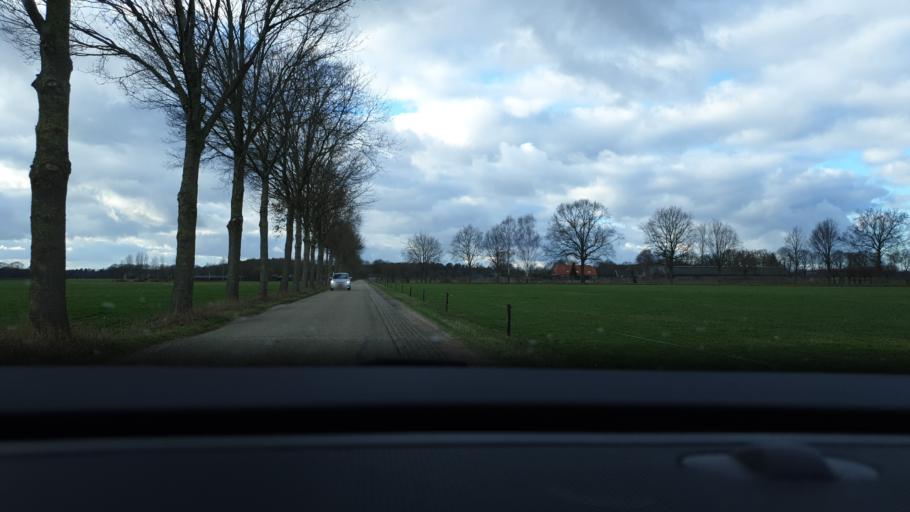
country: NL
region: Gelderland
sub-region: Oude IJsselstreek
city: Wisch
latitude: 51.9756
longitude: 6.3978
